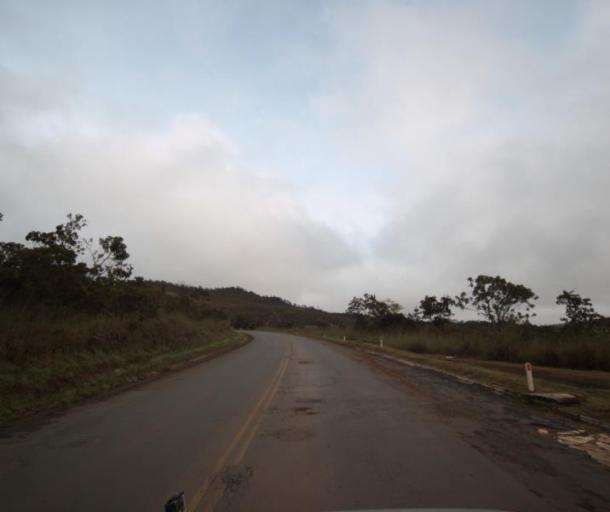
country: BR
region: Goias
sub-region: Pirenopolis
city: Pirenopolis
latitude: -15.8488
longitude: -48.7659
